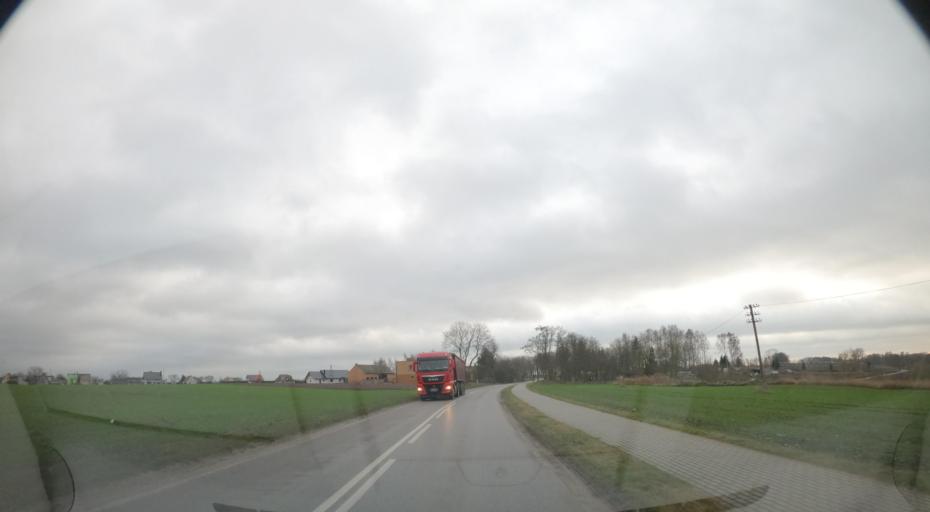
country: PL
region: Greater Poland Voivodeship
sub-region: Powiat pilski
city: Lobzenica
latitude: 53.2581
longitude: 17.2619
